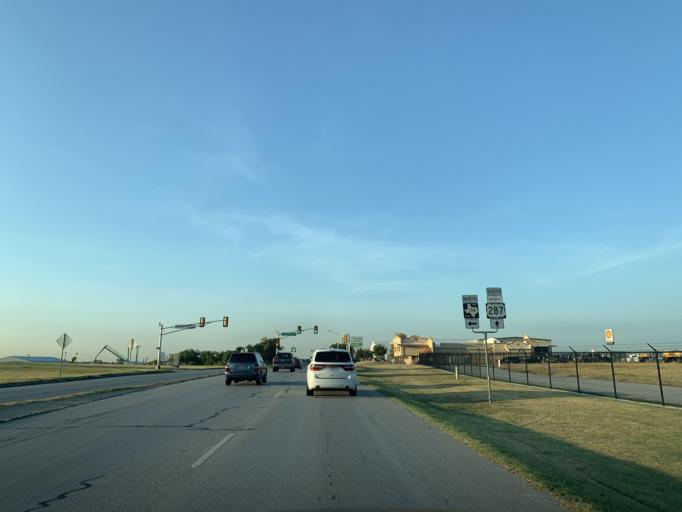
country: US
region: Texas
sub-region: Tarrant County
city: Blue Mound
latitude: 32.8171
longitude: -97.3515
